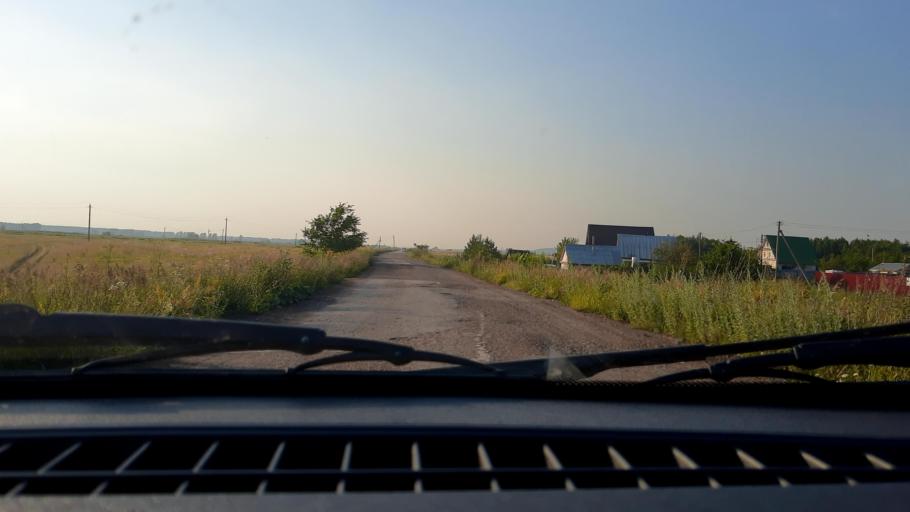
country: RU
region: Bashkortostan
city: Asanovo
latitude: 54.9162
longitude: 55.6272
